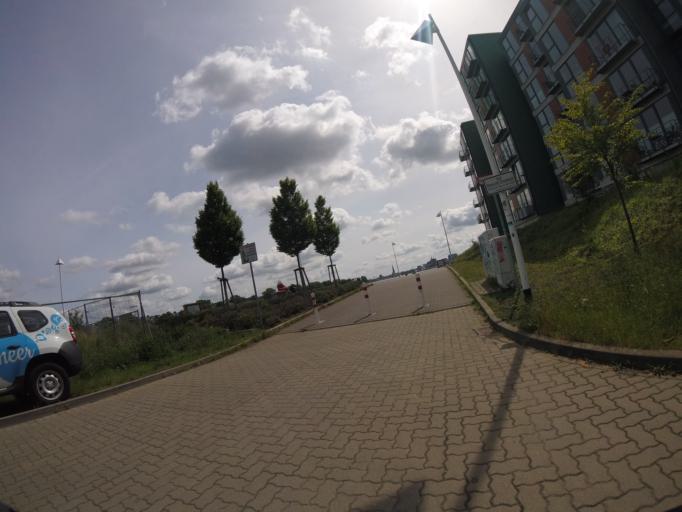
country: DE
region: Mecklenburg-Vorpommern
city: Rostock
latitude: 54.0977
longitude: 12.1072
